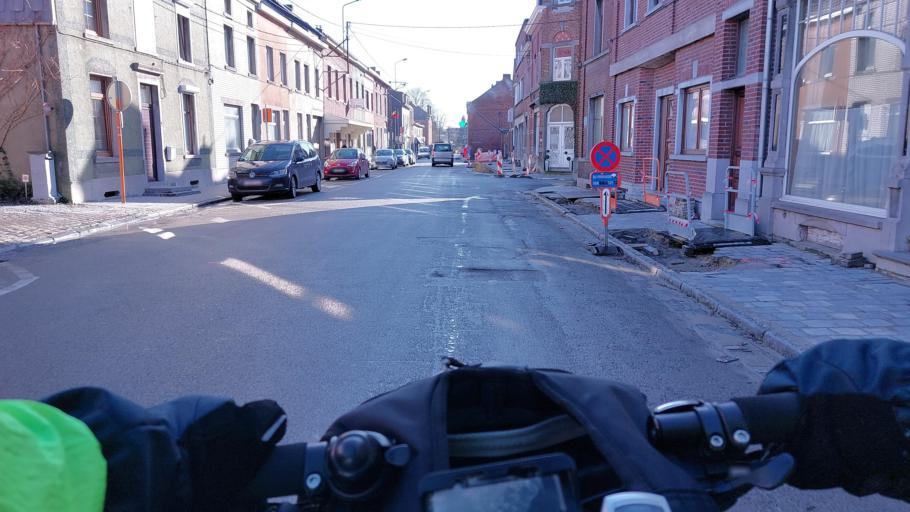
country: BE
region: Wallonia
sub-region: Province du Hainaut
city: Ecaussinnes-d'Enghien
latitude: 50.5622
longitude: 4.1537
